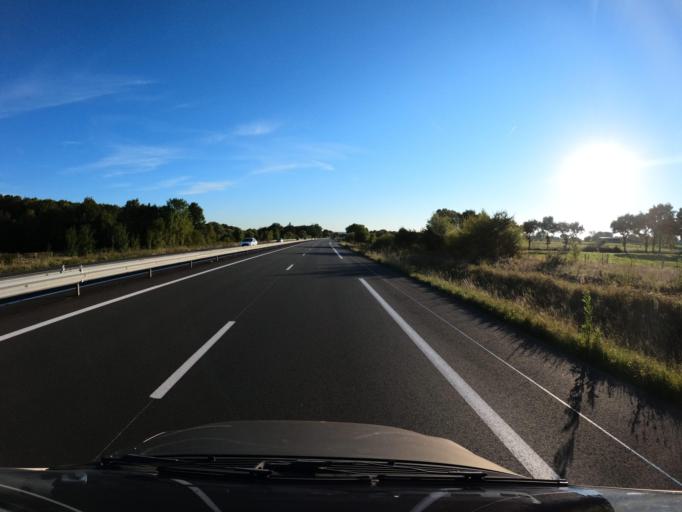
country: FR
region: Pays de la Loire
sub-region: Departement de la Vendee
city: Saint-Fulgent
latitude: 46.8515
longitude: -1.1452
